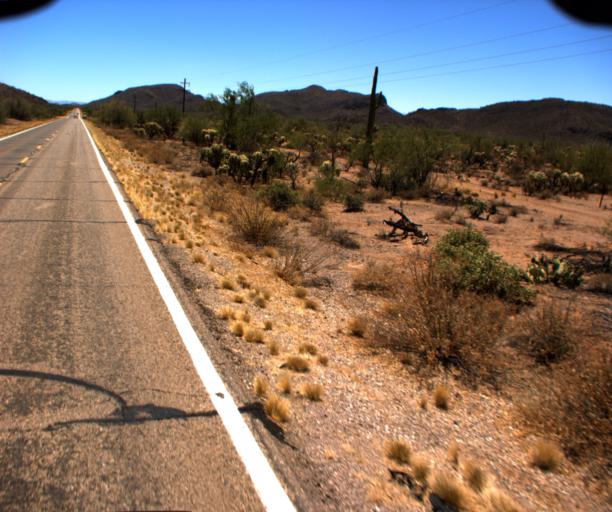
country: US
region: Arizona
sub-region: Pima County
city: Sells
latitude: 31.9766
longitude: -111.9654
